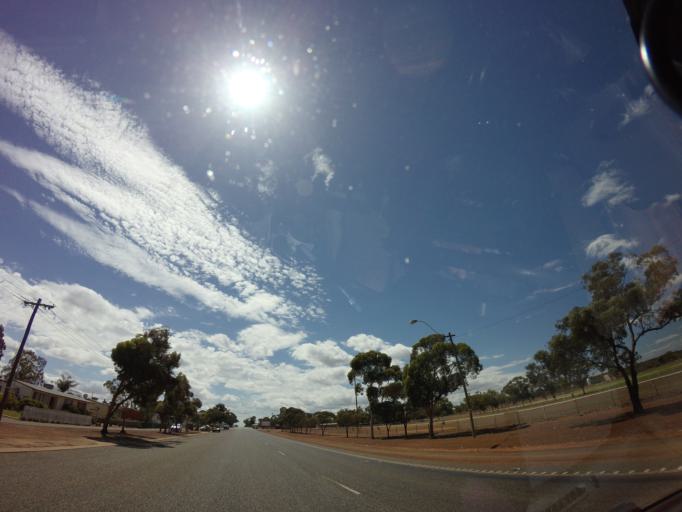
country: AU
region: Western Australia
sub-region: Kalgoorlie/Boulder
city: Boulder
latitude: -30.9546
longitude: 121.1563
